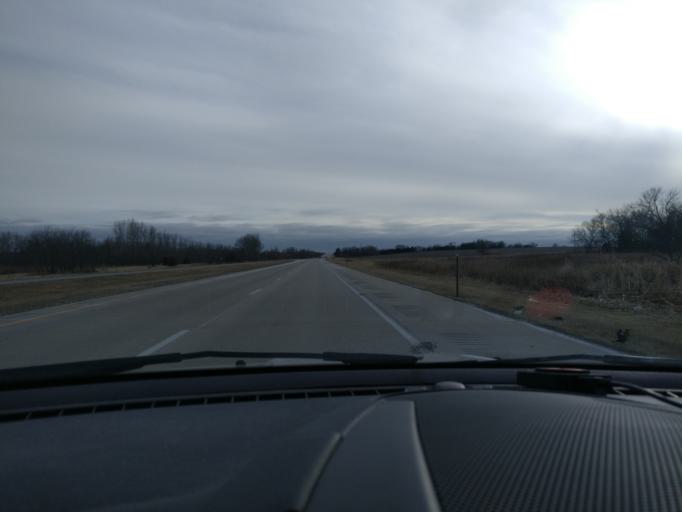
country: US
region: Nebraska
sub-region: Lancaster County
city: Waverly
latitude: 41.0250
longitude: -96.6406
